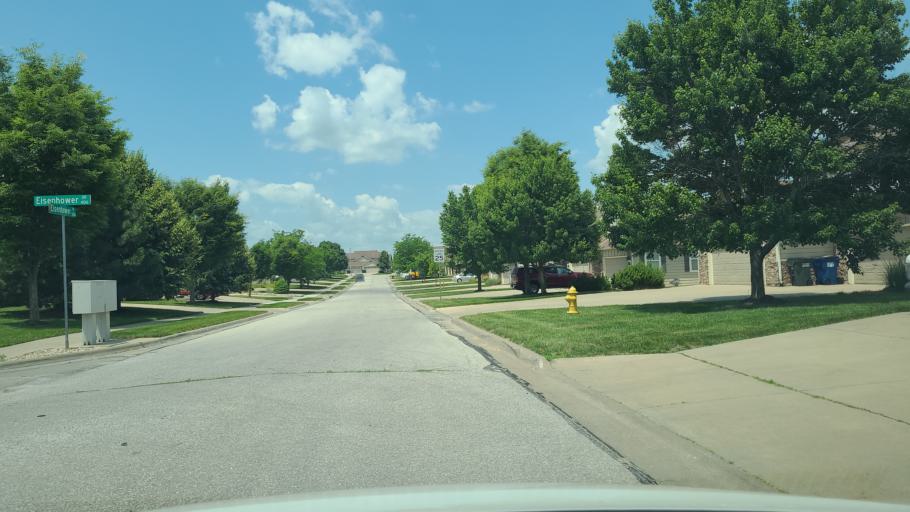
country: US
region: Kansas
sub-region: Douglas County
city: Lawrence
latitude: 38.9774
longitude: -95.3131
